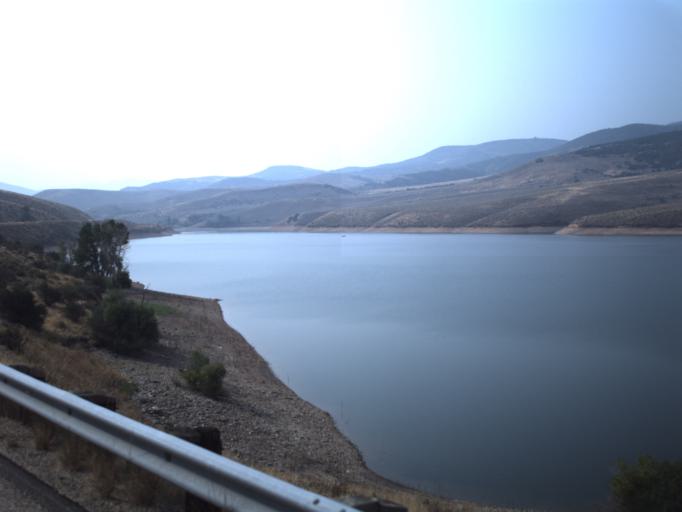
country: US
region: Utah
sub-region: Morgan County
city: Morgan
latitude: 40.9127
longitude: -111.5879
